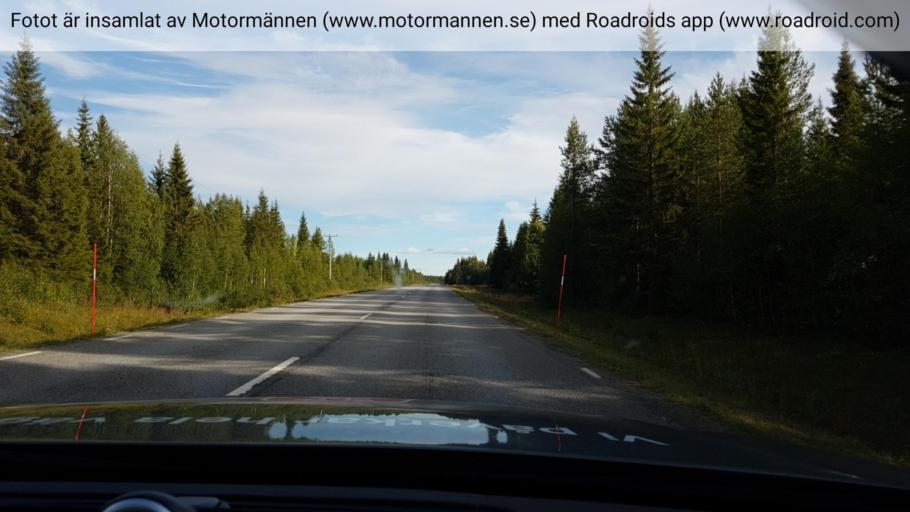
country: SE
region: Jaemtland
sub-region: Stroemsunds Kommun
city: Stroemsund
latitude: 64.2748
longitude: 15.3775
